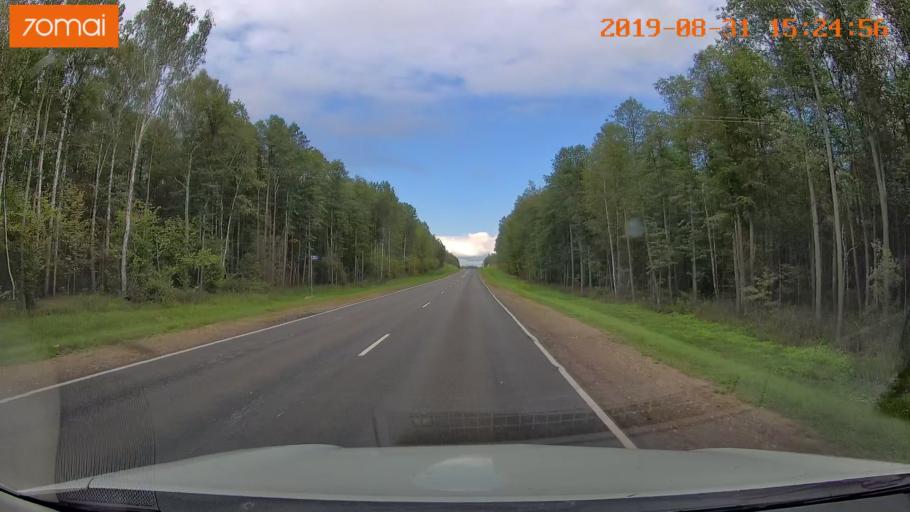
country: RU
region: Kaluga
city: Baryatino
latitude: 54.5345
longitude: 34.5121
